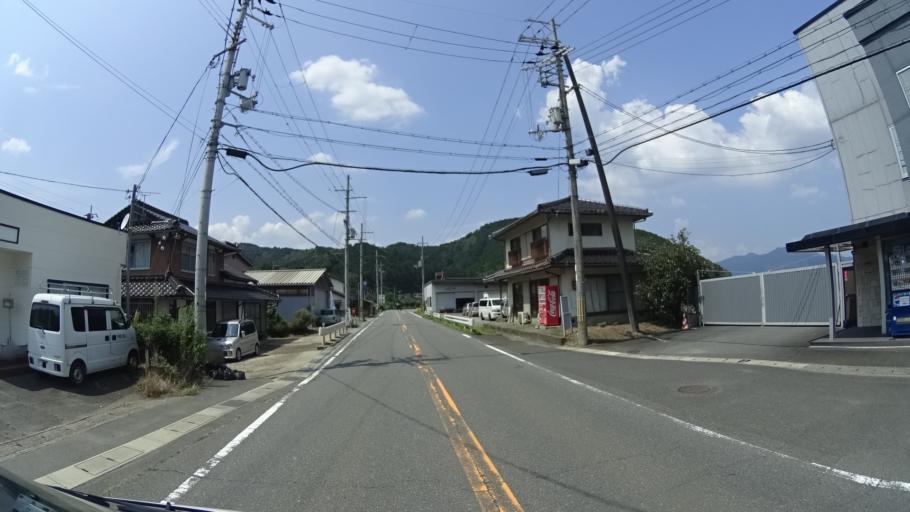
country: JP
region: Kyoto
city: Fukuchiyama
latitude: 35.2759
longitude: 135.1383
